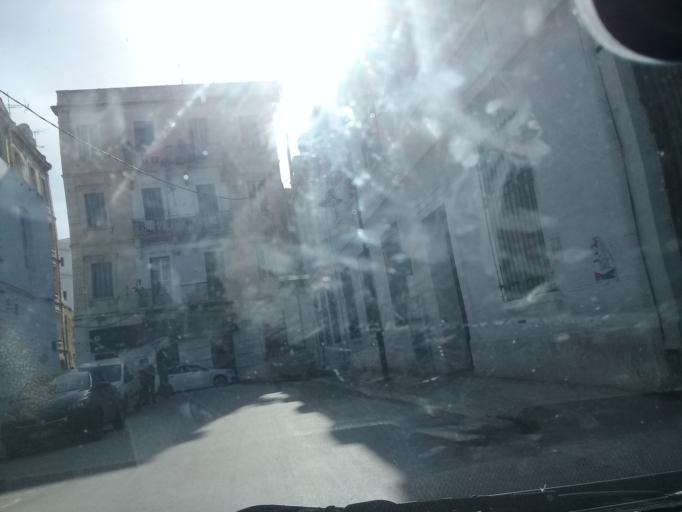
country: TN
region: Tunis
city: Tunis
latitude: 36.8017
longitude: 10.1805
